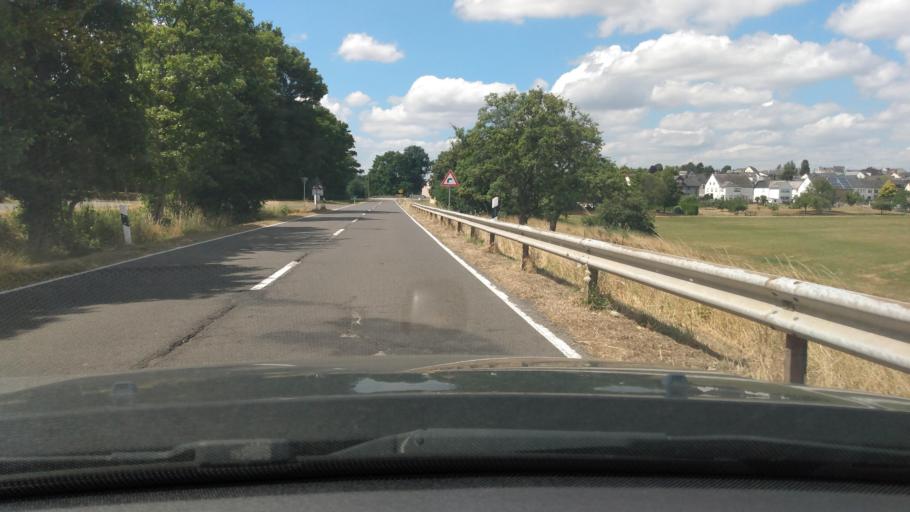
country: DE
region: Rheinland-Pfalz
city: Monzelfeld
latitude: 49.8889
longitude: 7.0797
